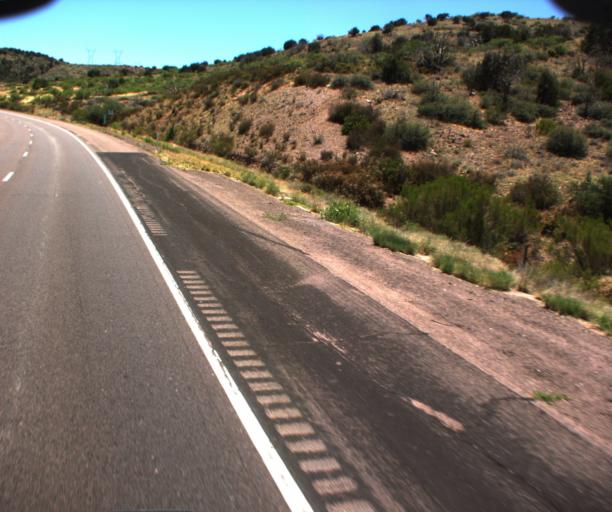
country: US
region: Arizona
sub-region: Gila County
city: Tonto Basin
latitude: 34.0143
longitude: -111.3597
